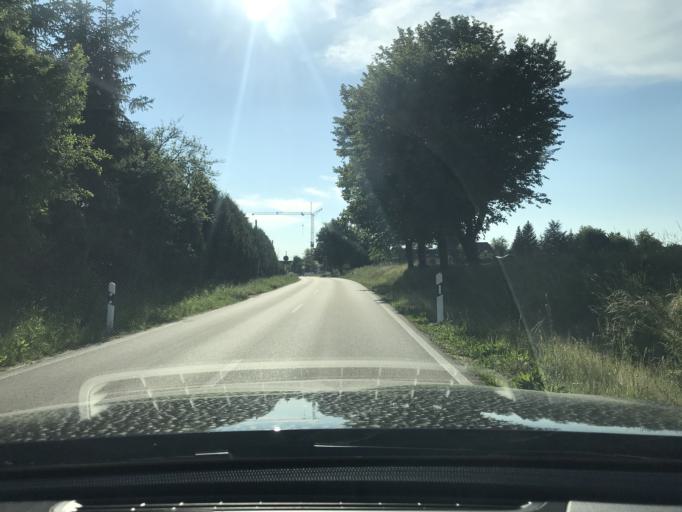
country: DE
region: Baden-Wuerttemberg
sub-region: Regierungsbezirk Stuttgart
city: Schwaikheim
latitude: 48.8909
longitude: 9.3258
